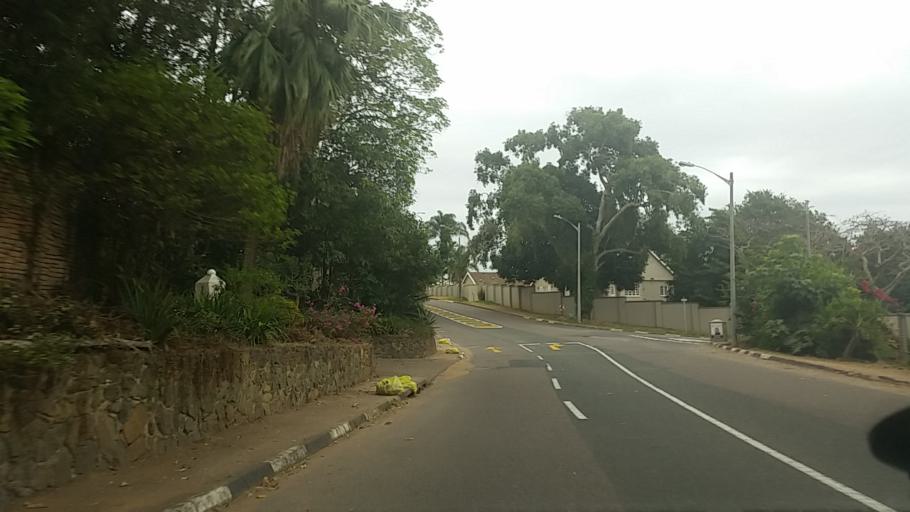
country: ZA
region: KwaZulu-Natal
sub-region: eThekwini Metropolitan Municipality
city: Berea
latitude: -29.8358
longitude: 30.9303
